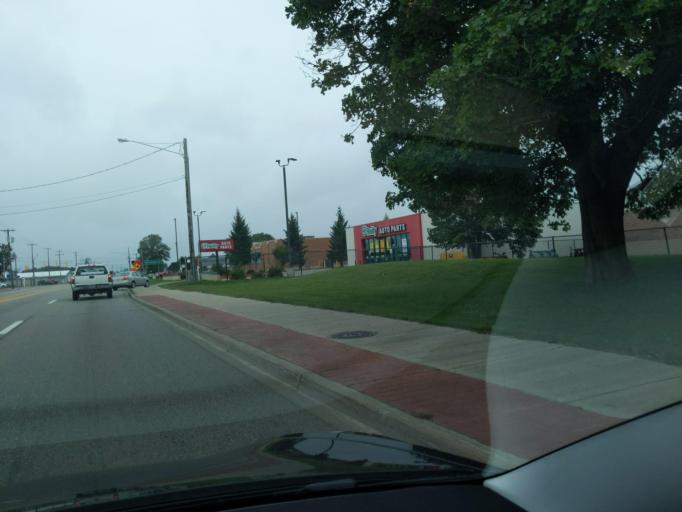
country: US
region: Michigan
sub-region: Wexford County
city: Cadillac
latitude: 44.2652
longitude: -85.4061
